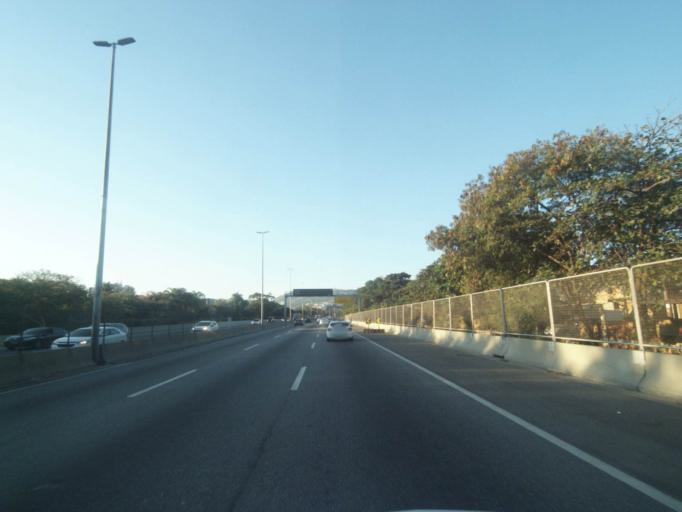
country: BR
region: Rio de Janeiro
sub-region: Sao Joao De Meriti
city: Sao Joao de Meriti
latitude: -22.9464
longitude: -43.3546
